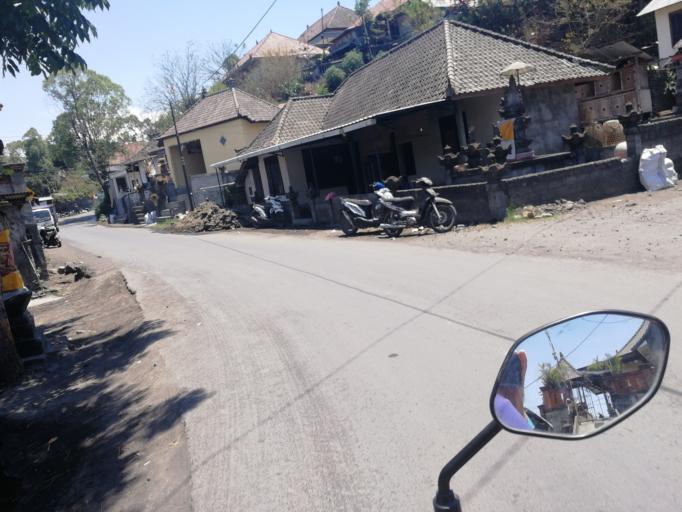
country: ID
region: Bali
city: Banjar Trunyan
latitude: -8.2287
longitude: 115.4093
